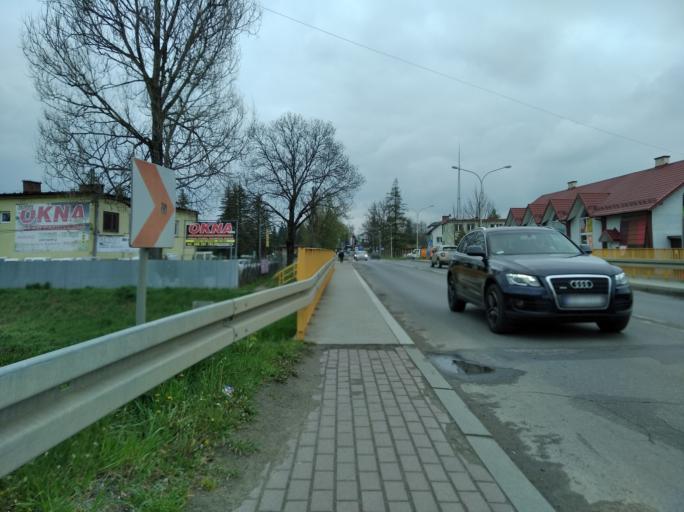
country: PL
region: Subcarpathian Voivodeship
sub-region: Powiat brzozowski
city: Brzozow
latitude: 49.7011
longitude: 22.0194
